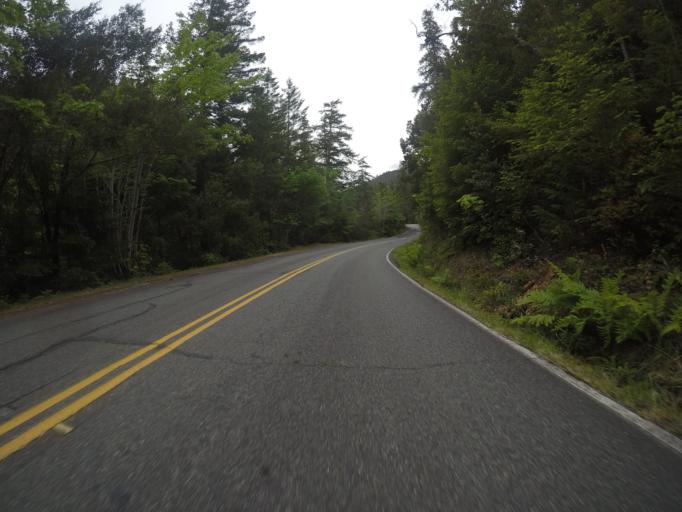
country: US
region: California
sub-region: Del Norte County
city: Bertsch-Oceanview
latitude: 41.7134
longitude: -123.9433
